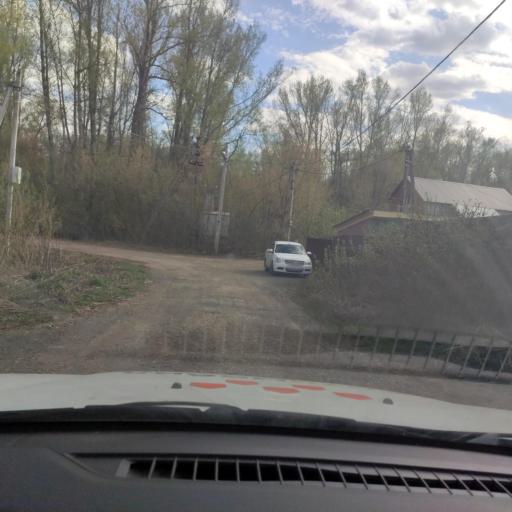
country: RU
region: Bashkortostan
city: Ufa
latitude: 54.7103
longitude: 55.9337
